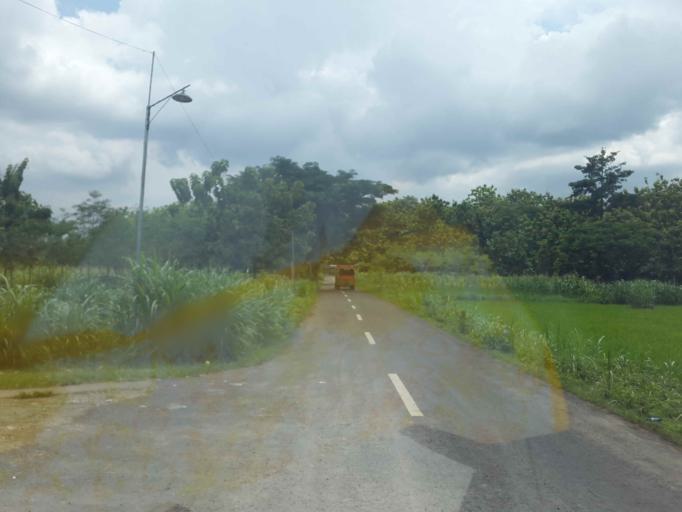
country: ID
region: Daerah Istimewa Yogyakarta
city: Wonosari
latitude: -7.9246
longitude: 110.6215
